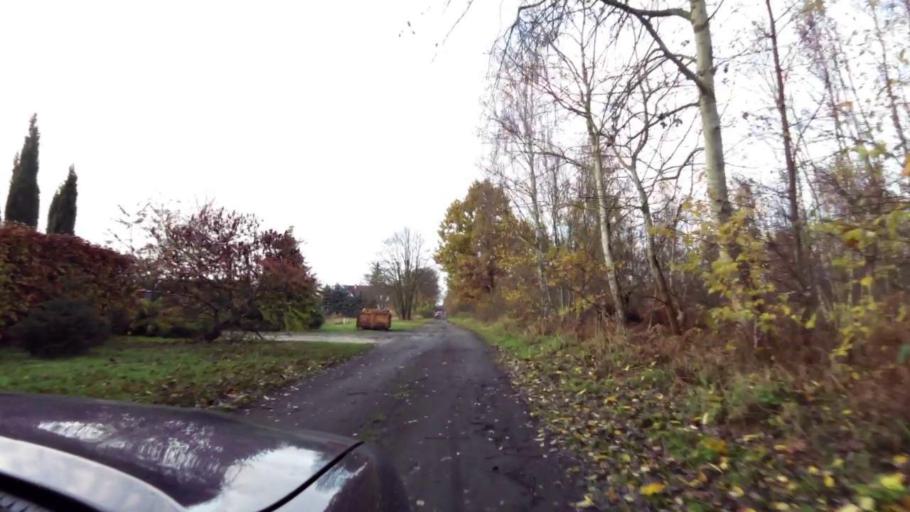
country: PL
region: West Pomeranian Voivodeship
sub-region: Powiat goleniowski
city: Goleniow
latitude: 53.5942
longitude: 14.7445
